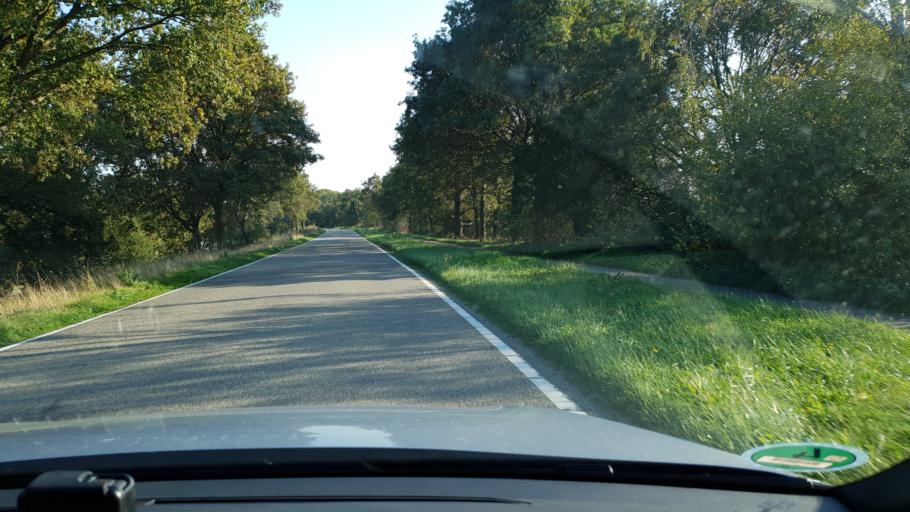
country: NL
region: North Brabant
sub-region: Gemeente Eindhoven
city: Meerhoven
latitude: 51.4639
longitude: 5.3936
